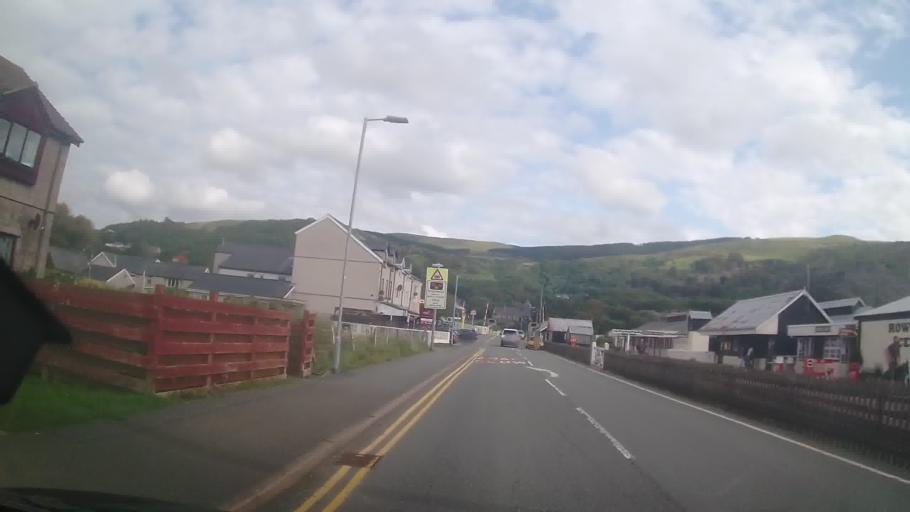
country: GB
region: Wales
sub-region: Gwynedd
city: Barmouth
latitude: 52.6962
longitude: -4.0510
